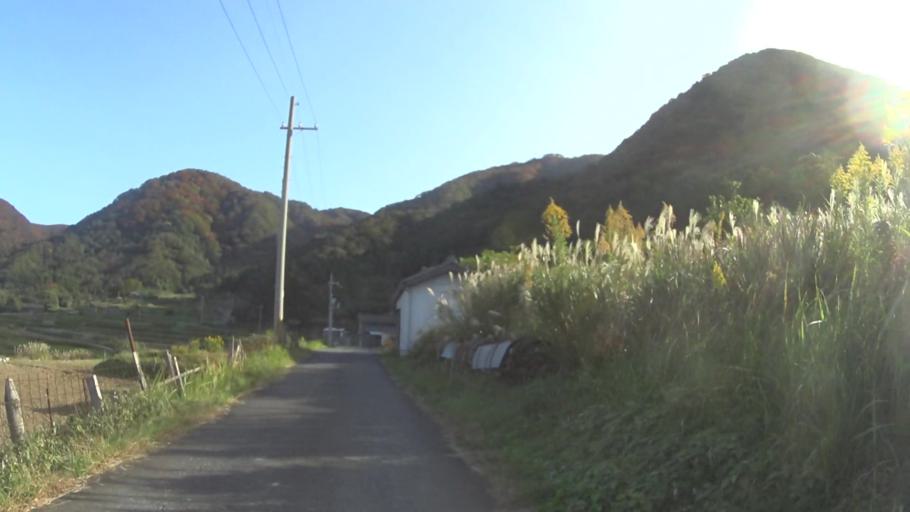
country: JP
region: Kyoto
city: Miyazu
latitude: 35.7630
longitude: 135.1996
